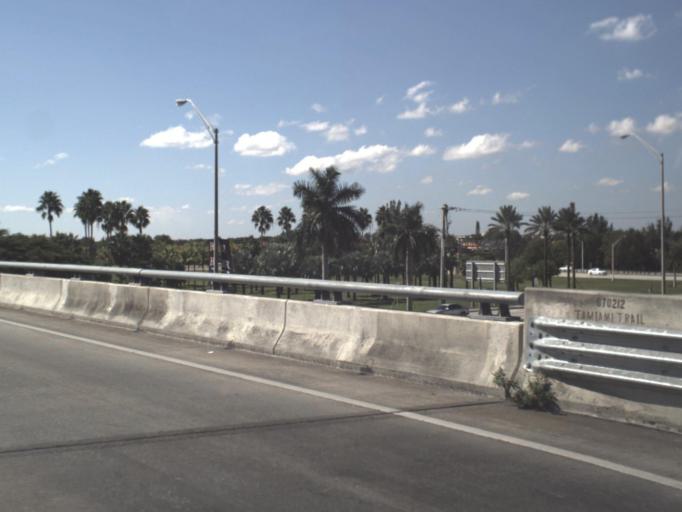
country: US
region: Florida
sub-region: Miami-Dade County
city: Sweetwater
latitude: 25.7616
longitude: -80.3855
